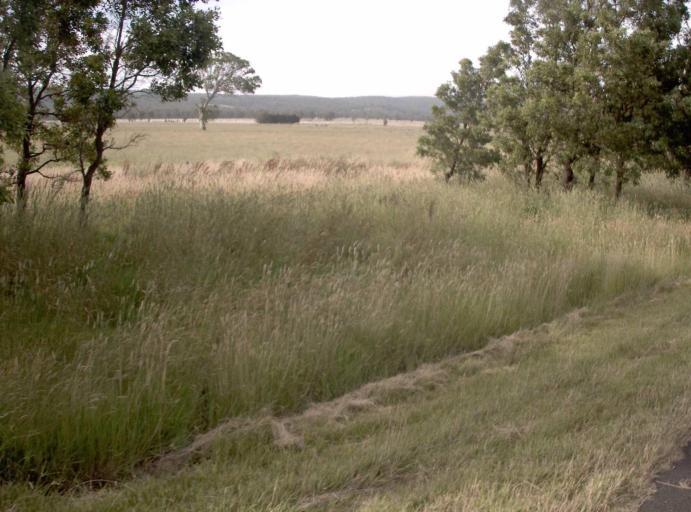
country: AU
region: Victoria
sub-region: Latrobe
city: Traralgon
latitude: -38.0877
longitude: 146.6034
